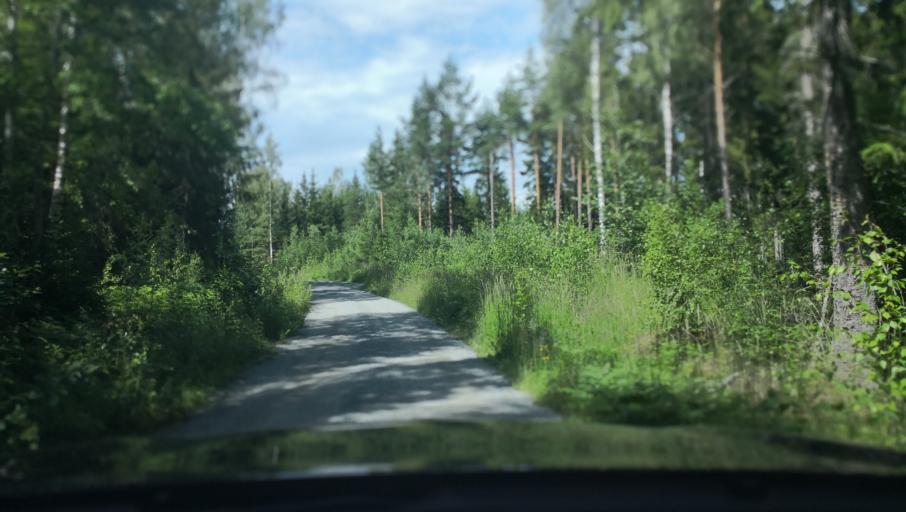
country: SE
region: Vaestmanland
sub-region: Surahammars Kommun
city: Ramnas
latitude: 59.9406
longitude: 16.1911
